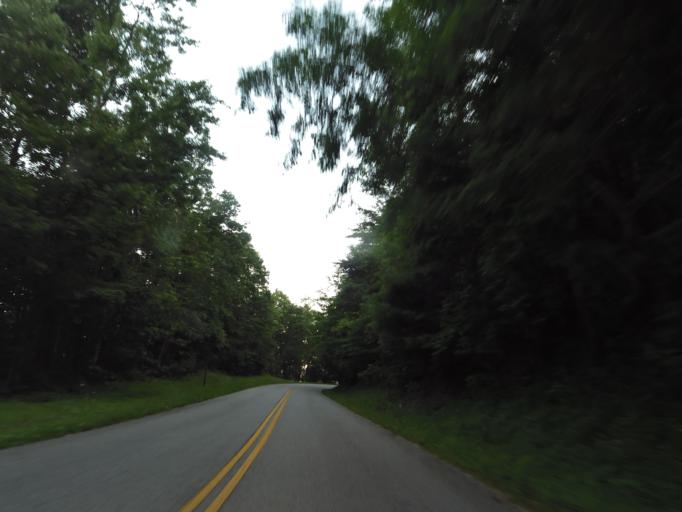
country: US
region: Tennessee
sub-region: Blount County
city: Maryville
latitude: 35.6280
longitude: -83.9496
